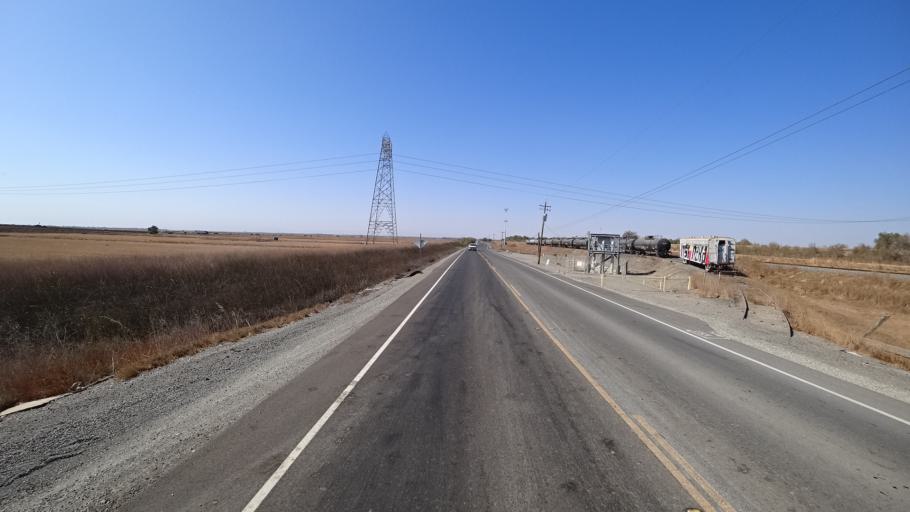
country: US
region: California
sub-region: Yolo County
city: Woodland
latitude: 38.6767
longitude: -121.6730
